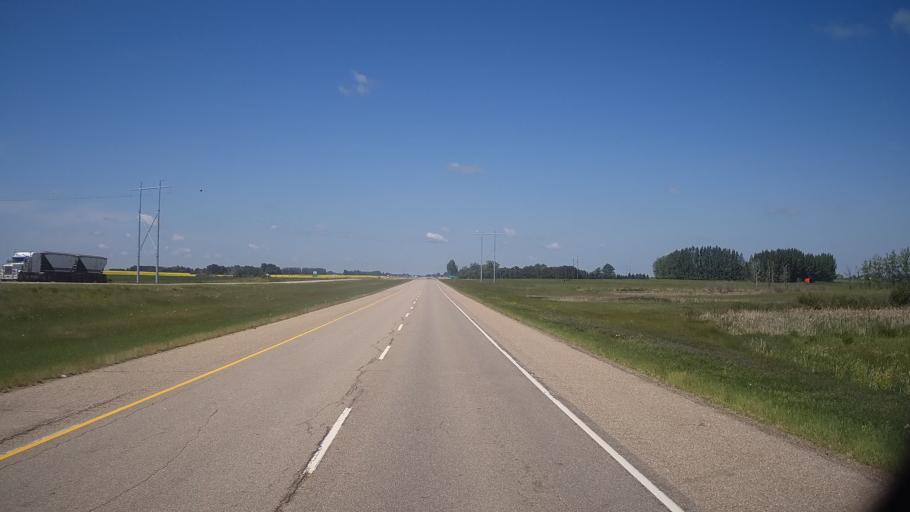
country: CA
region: Saskatchewan
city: Saskatoon
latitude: 51.9981
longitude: -106.3043
